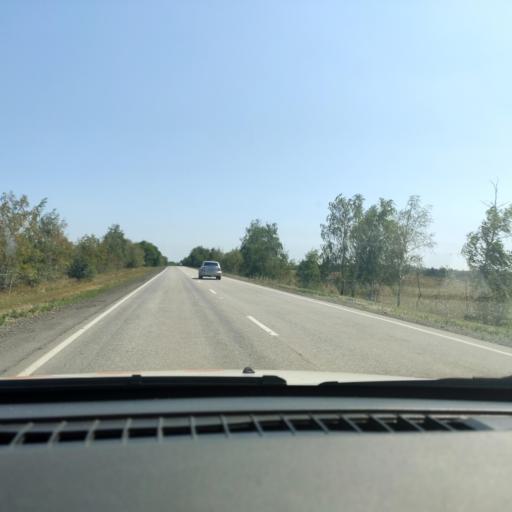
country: RU
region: Voronezj
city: Ostrogozhsk
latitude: 50.8023
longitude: 39.3212
